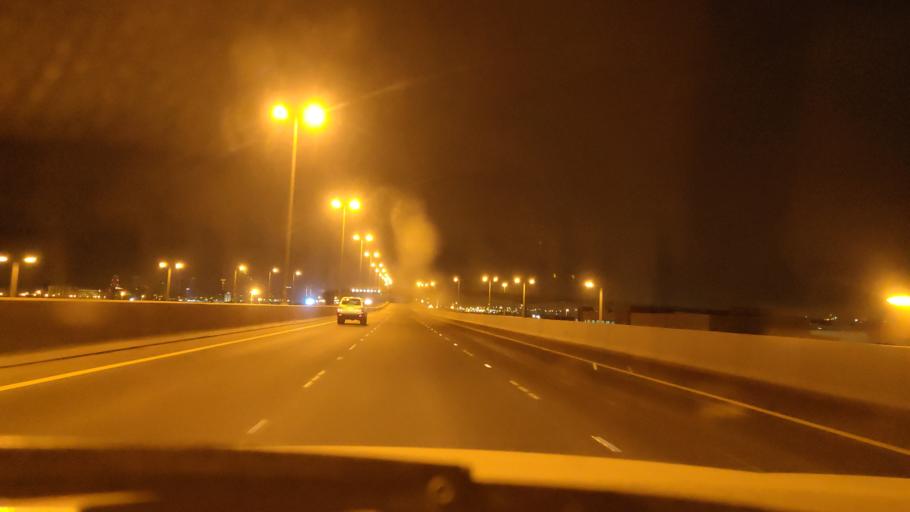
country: KW
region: Al Asimah
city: Ar Rabiyah
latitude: 29.3293
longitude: 47.9256
